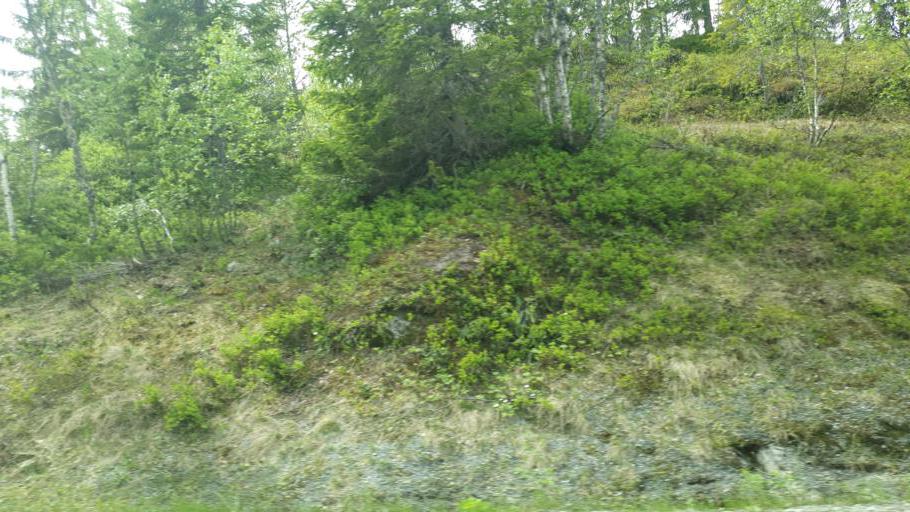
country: NO
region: Nord-Trondelag
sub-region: Leksvik
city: Leksvik
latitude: 63.6927
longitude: 10.4502
